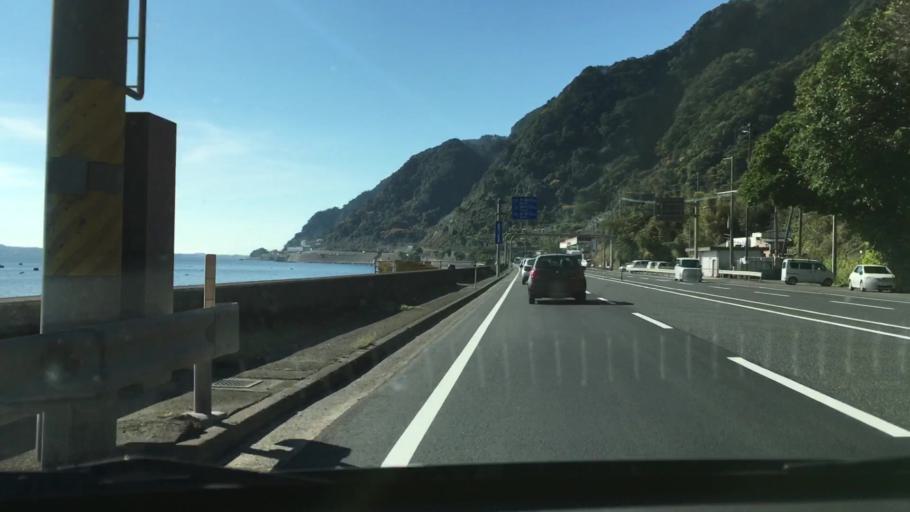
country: JP
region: Kagoshima
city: Kagoshima-shi
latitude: 31.6490
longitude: 130.6056
